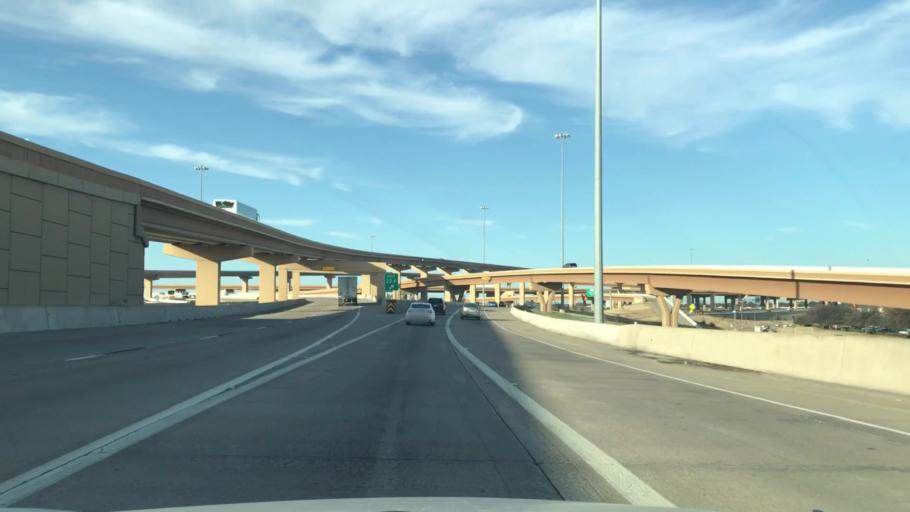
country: US
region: Texas
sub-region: Tarrant County
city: North Richland Hills
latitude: 32.8271
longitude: -97.2052
